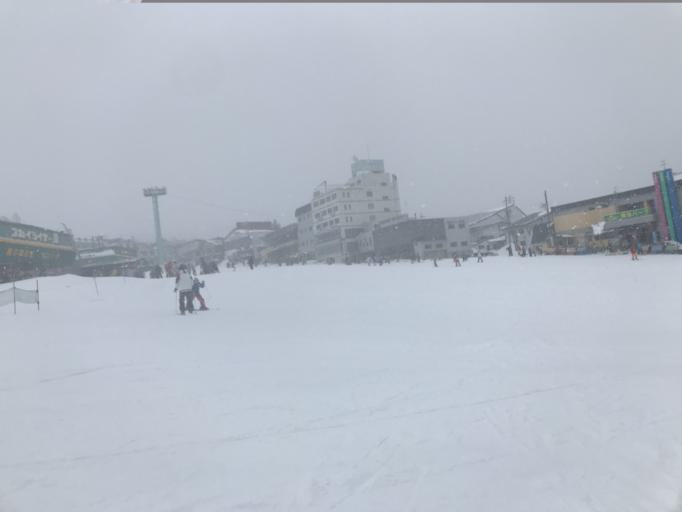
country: JP
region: Nagano
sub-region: Kitaazumi Gun
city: Hakuba
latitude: 36.7464
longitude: 137.8688
